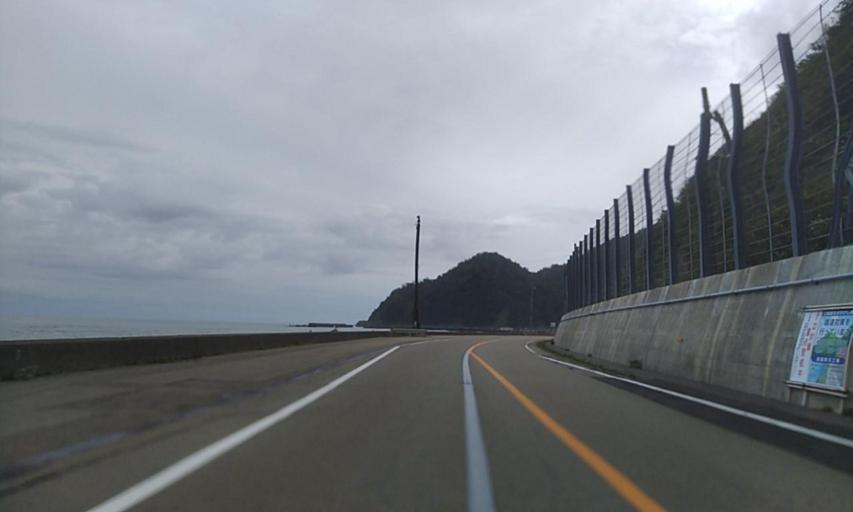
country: JP
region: Hokkaido
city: Obihiro
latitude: 42.1297
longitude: 143.3175
